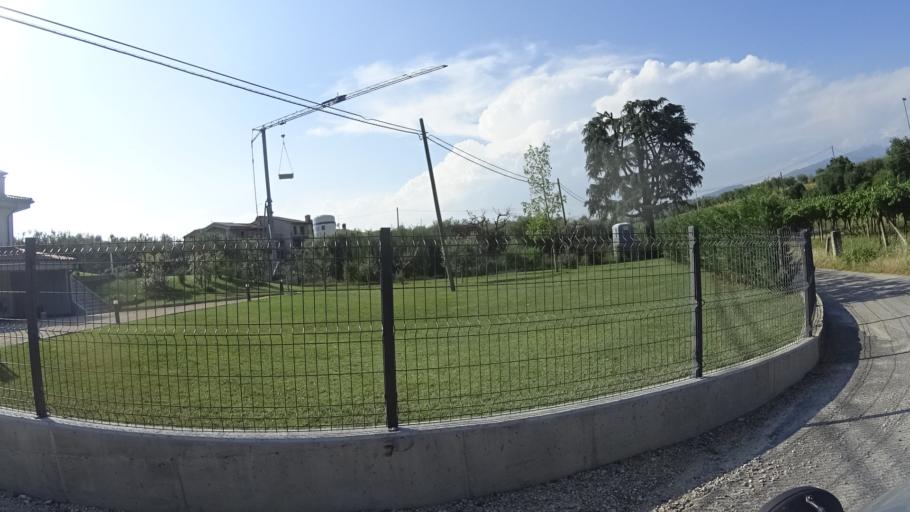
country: IT
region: Veneto
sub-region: Provincia di Verona
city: Calmasino
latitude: 45.5147
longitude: 10.7649
